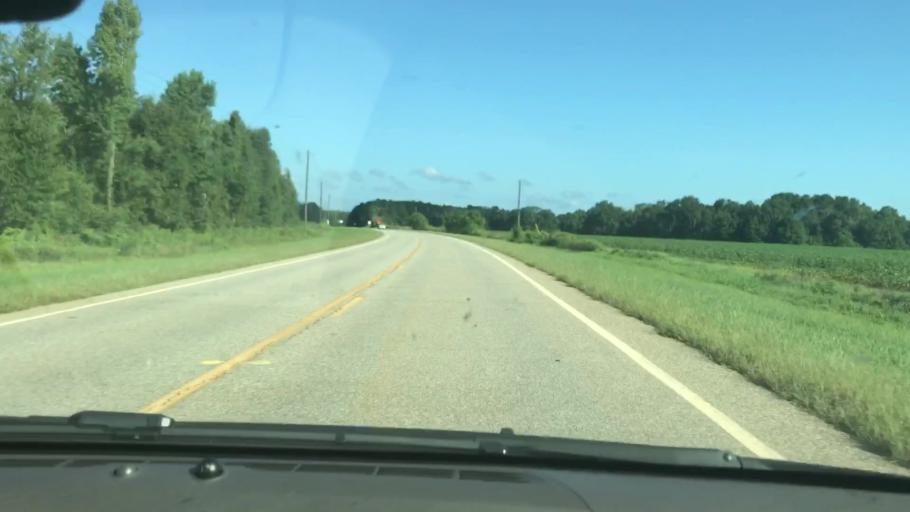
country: US
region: Georgia
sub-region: Clay County
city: Fort Gaines
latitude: 31.7362
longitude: -85.0485
